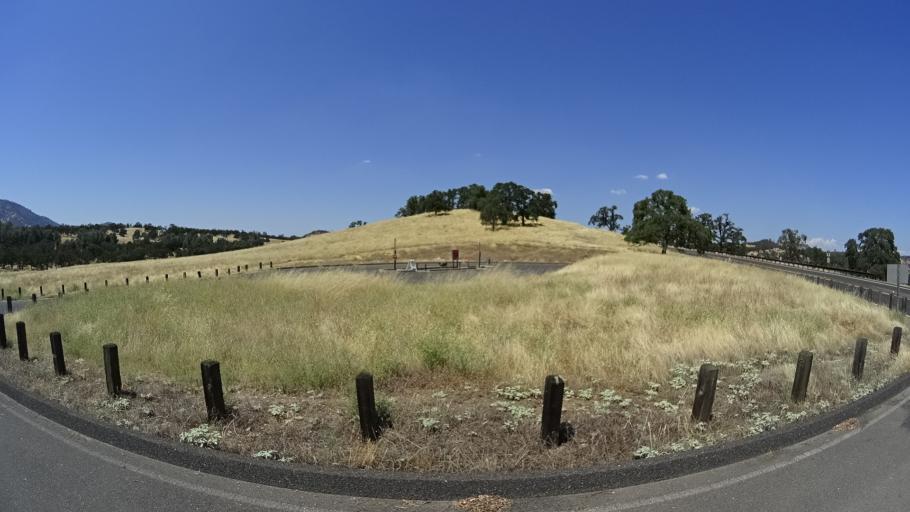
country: US
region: California
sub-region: Calaveras County
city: Angels Camp
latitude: 38.0153
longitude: -120.5256
